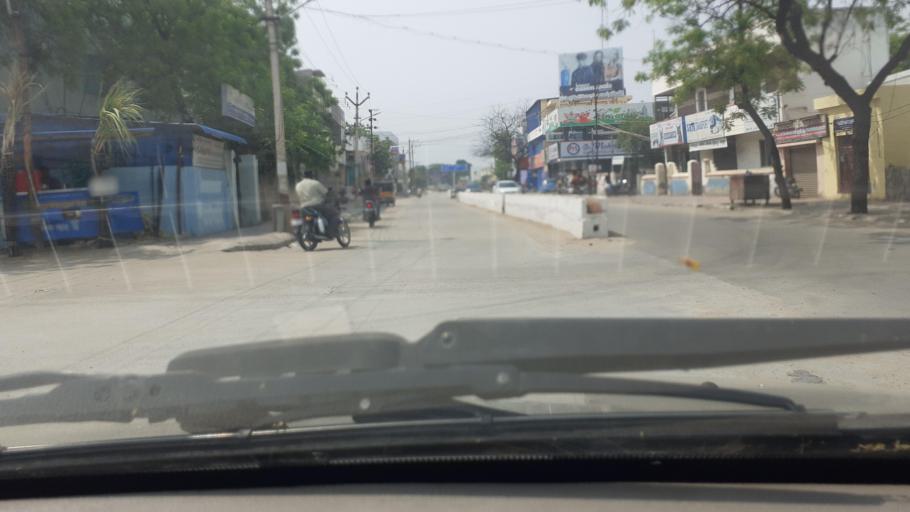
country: IN
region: Tamil Nadu
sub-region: Thoothukkudi
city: Korampallam
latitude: 8.8058
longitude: 78.1388
